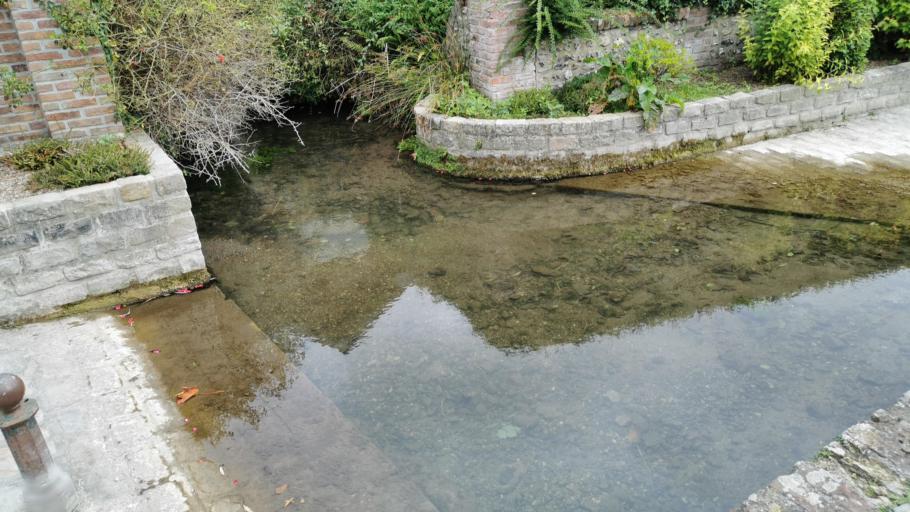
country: FR
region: Haute-Normandie
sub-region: Departement de la Seine-Maritime
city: Martin-Eglise
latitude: 49.9000
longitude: 1.1418
